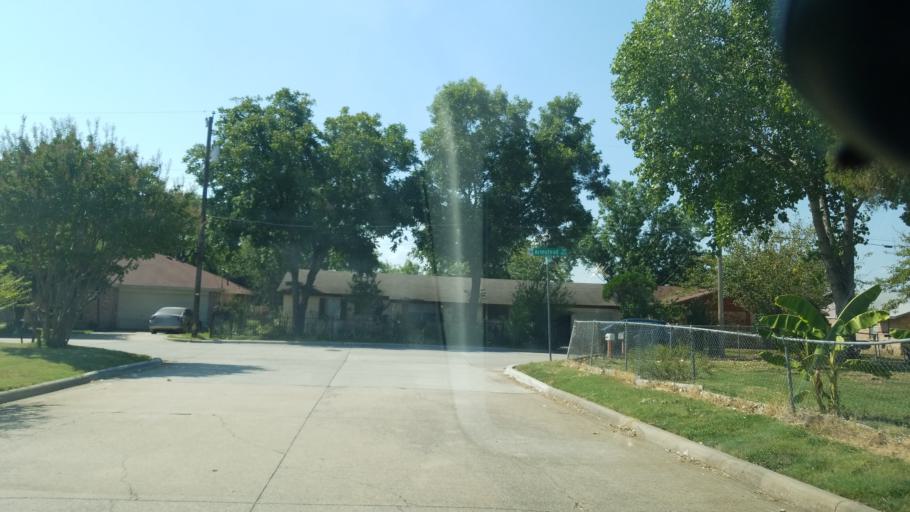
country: US
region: Texas
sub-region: Dallas County
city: Grand Prairie
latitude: 32.7082
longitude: -96.9799
